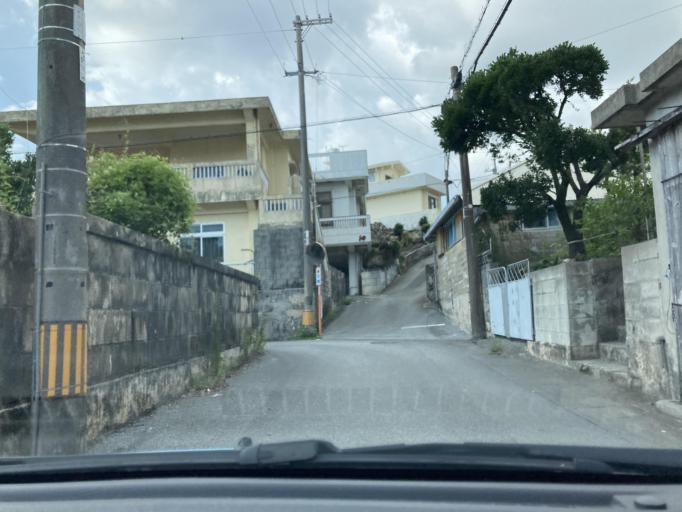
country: JP
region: Okinawa
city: Itoman
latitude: 26.1313
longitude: 127.7722
